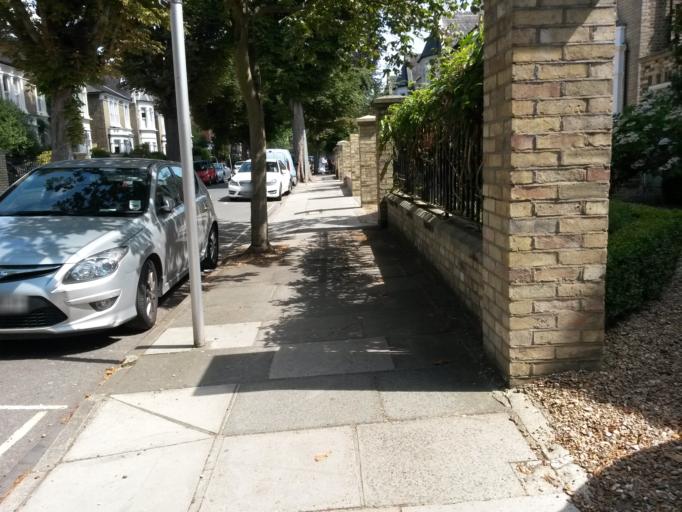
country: GB
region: England
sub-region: Greater London
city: Richmond
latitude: 51.4775
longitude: -0.2881
